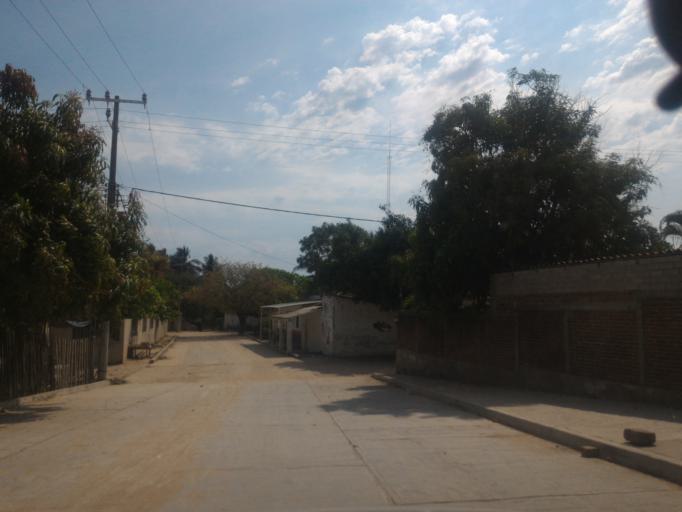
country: MX
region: Michoacan
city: Coahuayana Viejo
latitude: 18.2975
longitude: -103.4100
